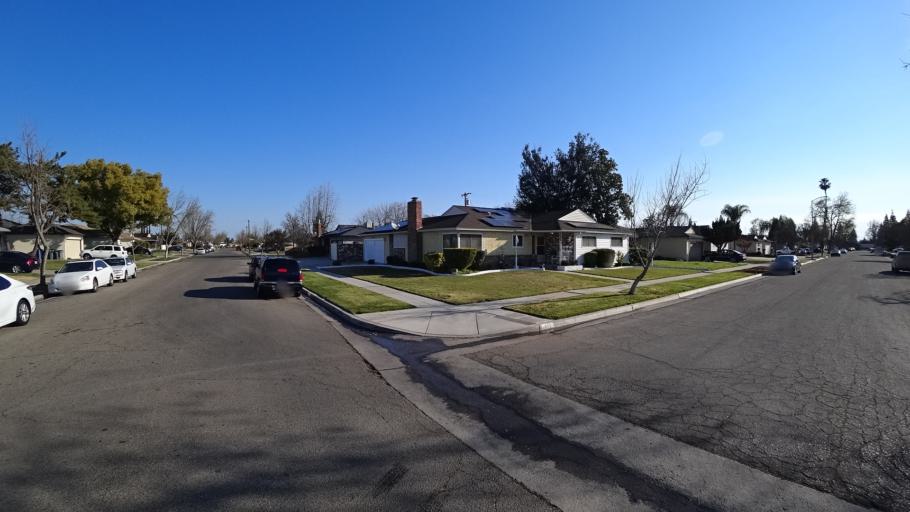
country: US
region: California
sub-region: Fresno County
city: Fresno
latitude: 36.8167
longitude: -119.7759
